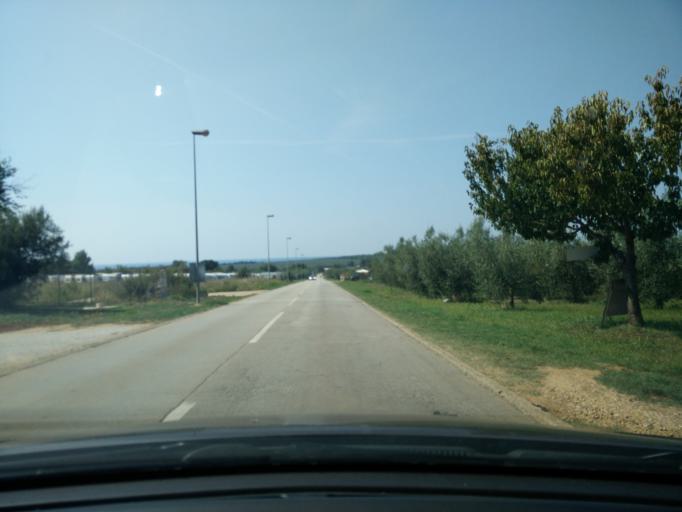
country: HR
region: Istarska
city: Novigrad
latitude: 45.2950
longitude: 13.6104
